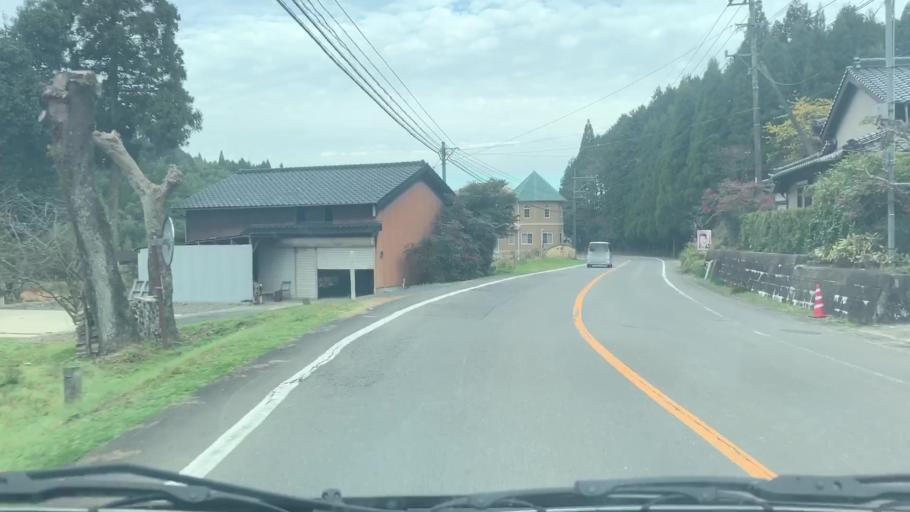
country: JP
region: Saga Prefecture
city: Takeocho-takeo
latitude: 33.1884
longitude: 129.9670
